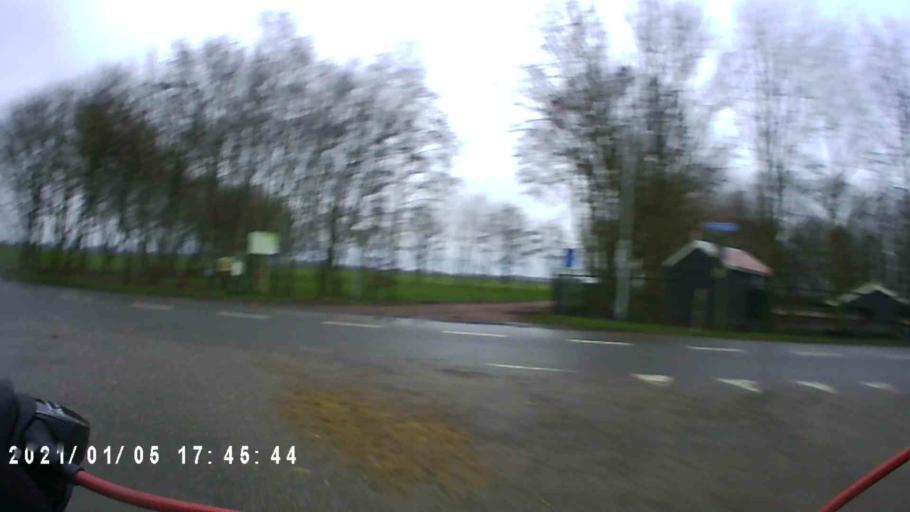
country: NL
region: Groningen
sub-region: Gemeente Veendam
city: Veendam
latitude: 53.2077
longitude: 6.9128
